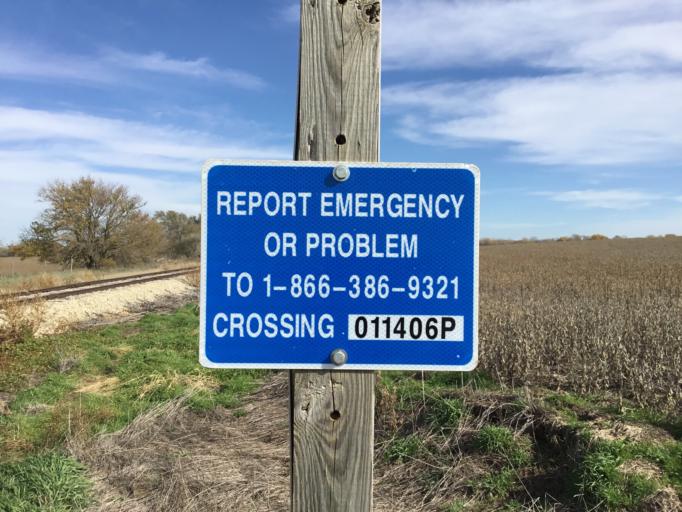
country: US
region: Kansas
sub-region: Lincoln County
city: Lincoln
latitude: 38.9156
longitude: -97.9473
